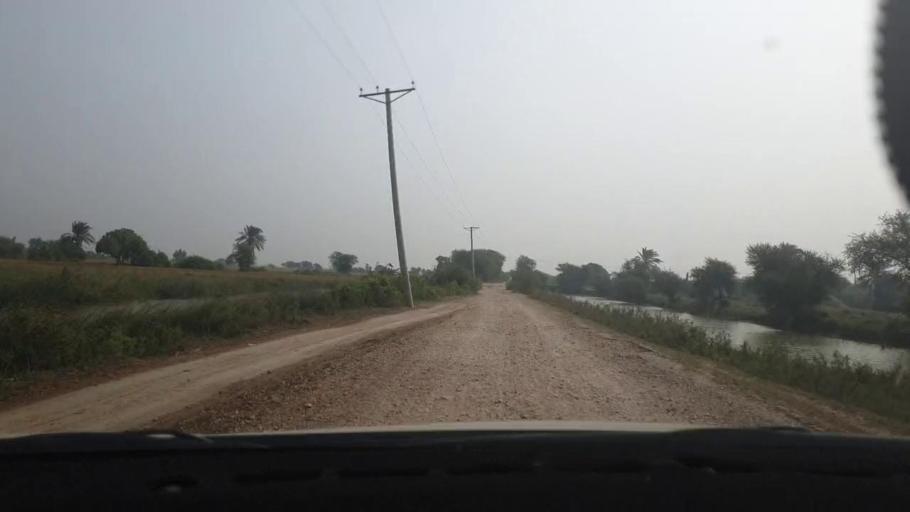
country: PK
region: Sindh
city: Tando Muhammad Khan
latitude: 25.0746
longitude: 68.4988
